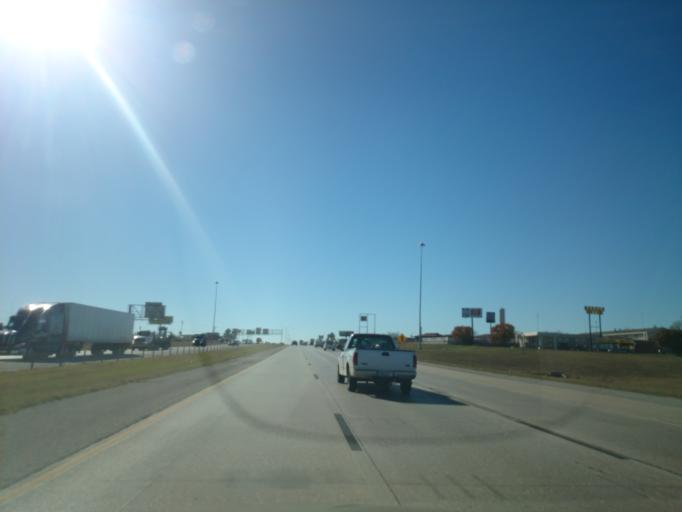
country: US
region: Oklahoma
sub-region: Oklahoma County
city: Edmond
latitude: 35.5931
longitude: -97.4340
